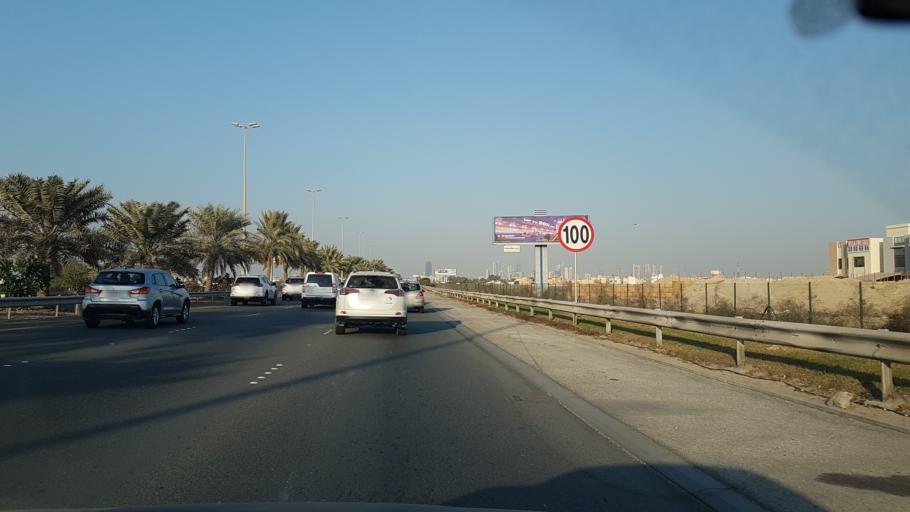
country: BH
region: Manama
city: Jidd Hafs
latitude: 26.1993
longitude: 50.5101
